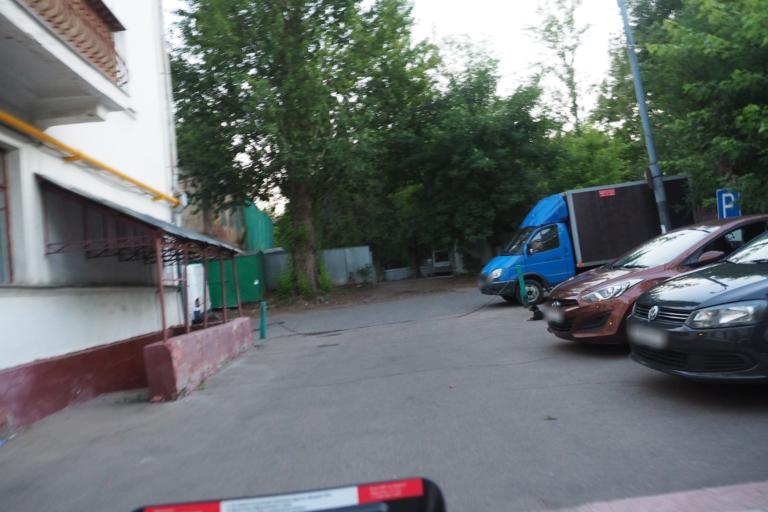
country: RU
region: Moscow
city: Kotlovka
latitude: 55.6821
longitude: 37.6100
